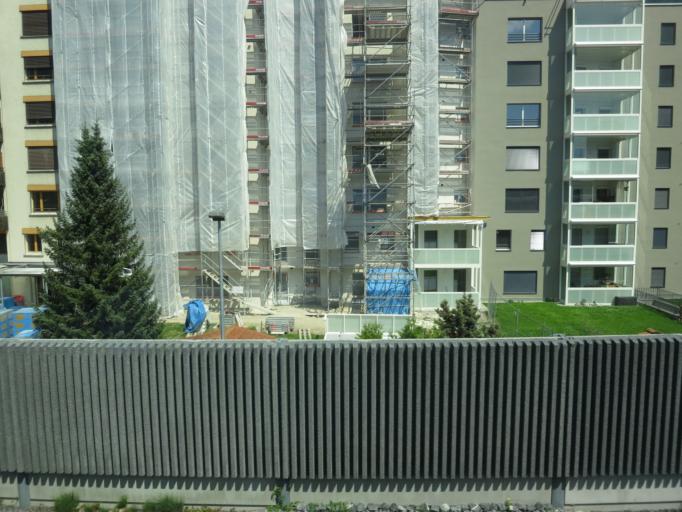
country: CH
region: Grisons
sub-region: Plessur District
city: Chur
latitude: 46.8624
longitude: 9.5315
